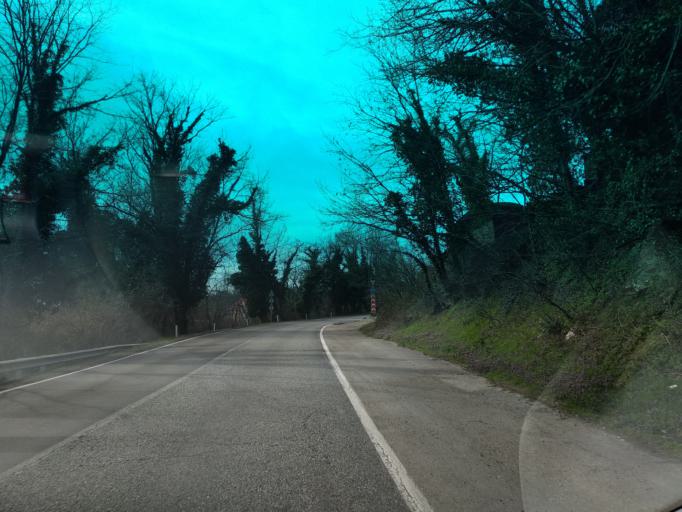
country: RU
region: Krasnodarskiy
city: Shepsi
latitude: 44.0827
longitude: 39.1318
